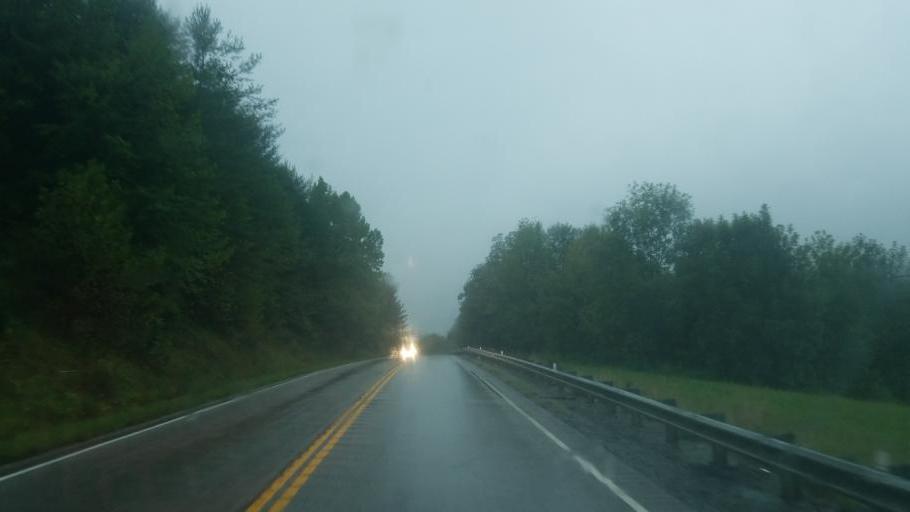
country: US
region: Kentucky
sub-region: Rowan County
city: Morehead
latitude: 38.3050
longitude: -83.5683
